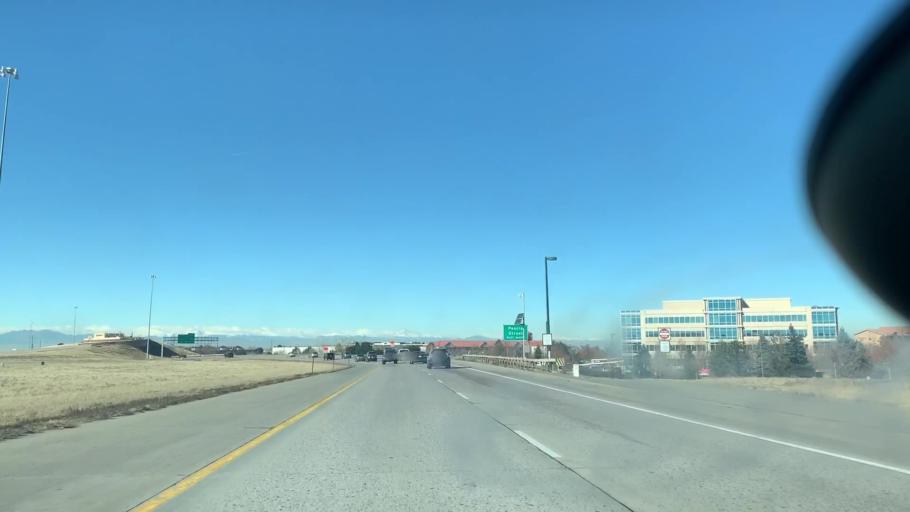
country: US
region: Colorado
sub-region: Adams County
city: Aurora
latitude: 39.7694
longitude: -104.7990
